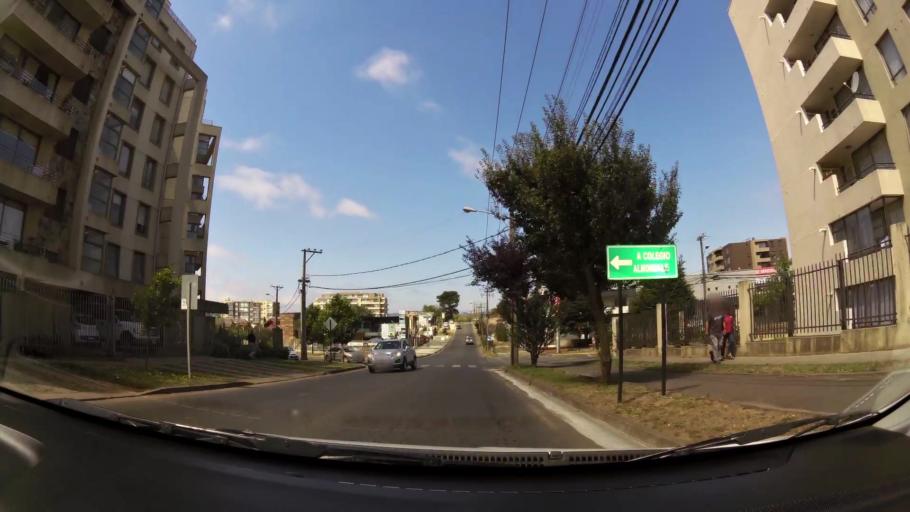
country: CL
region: Biobio
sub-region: Provincia de Concepcion
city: Concepcion
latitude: -36.7806
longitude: -73.0451
